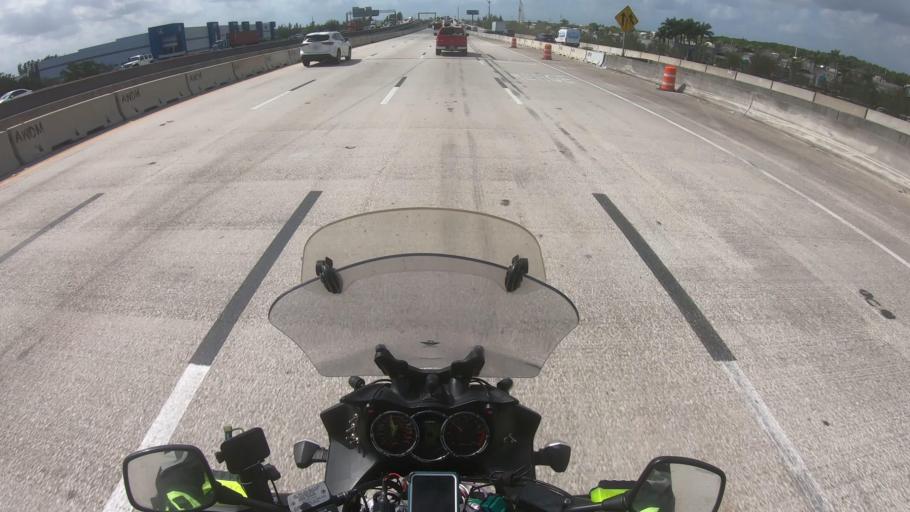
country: US
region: Florida
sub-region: Broward County
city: Melrose Park
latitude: 26.0850
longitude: -80.1758
